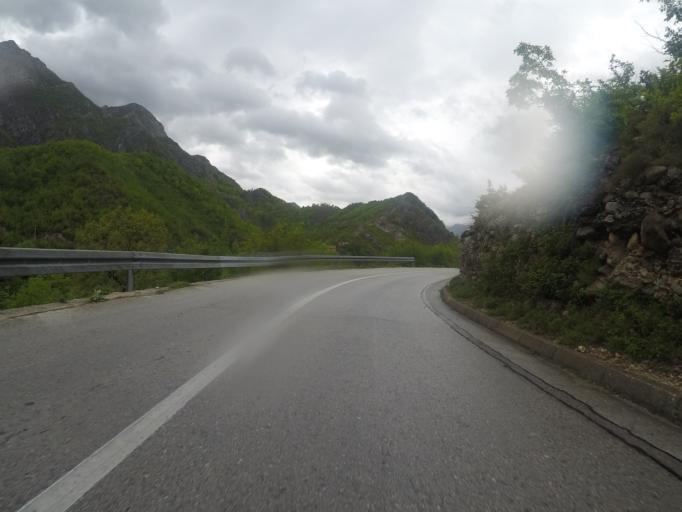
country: BA
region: Federation of Bosnia and Herzegovina
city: Siroki Brijeg
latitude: 43.5341
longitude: 17.6565
